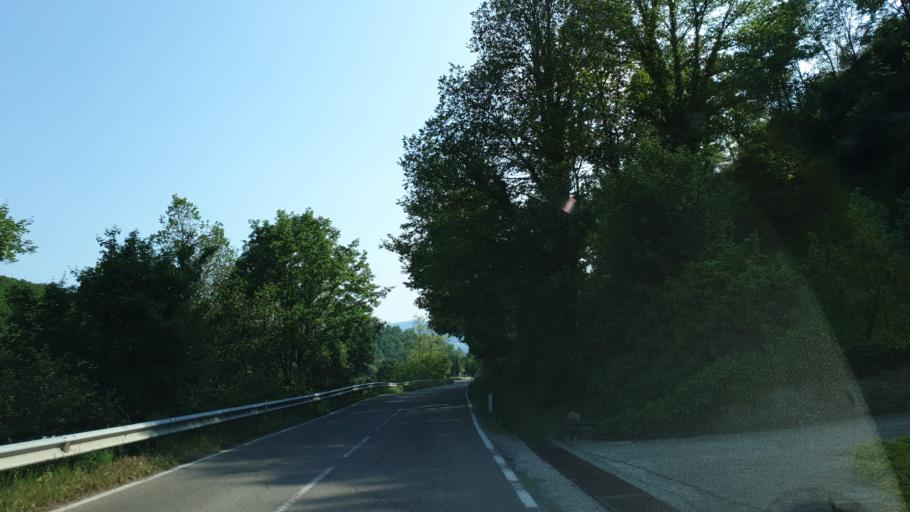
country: IT
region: Tuscany
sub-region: Province of Arezzo
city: Soci
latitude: 43.7559
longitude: 11.8279
